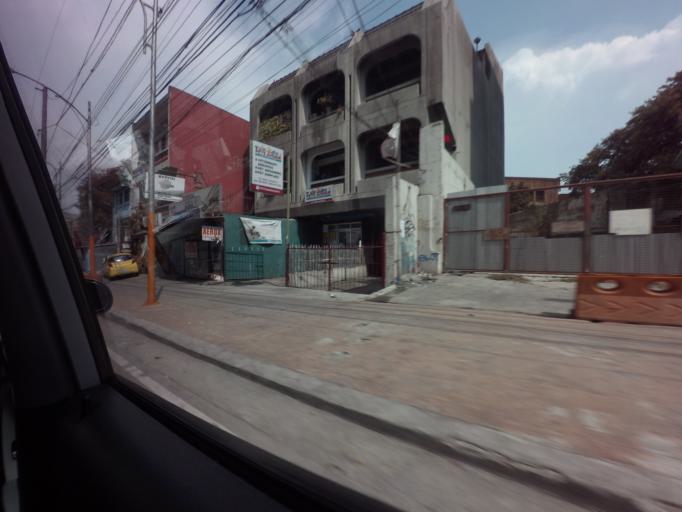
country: PH
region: Metro Manila
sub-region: San Juan
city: San Juan
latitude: 14.6022
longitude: 121.0139
